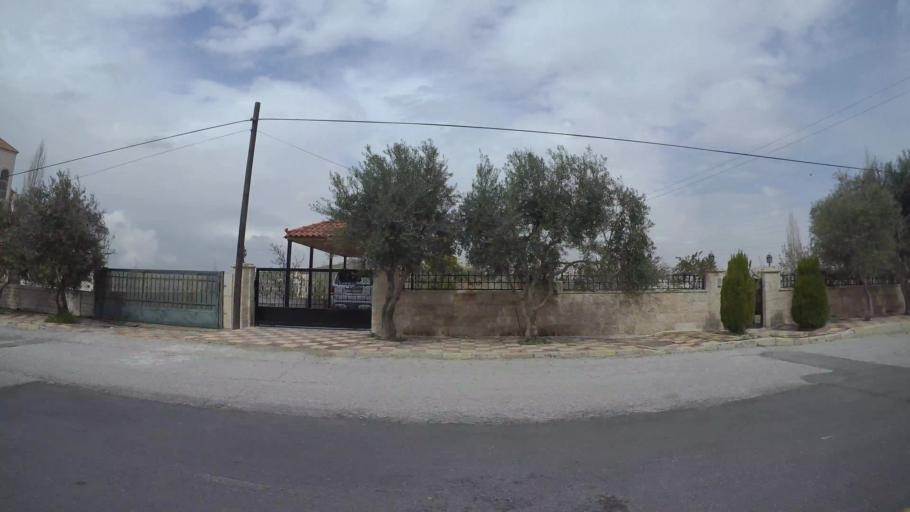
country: JO
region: Amman
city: Umm as Summaq
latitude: 31.8980
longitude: 35.8321
